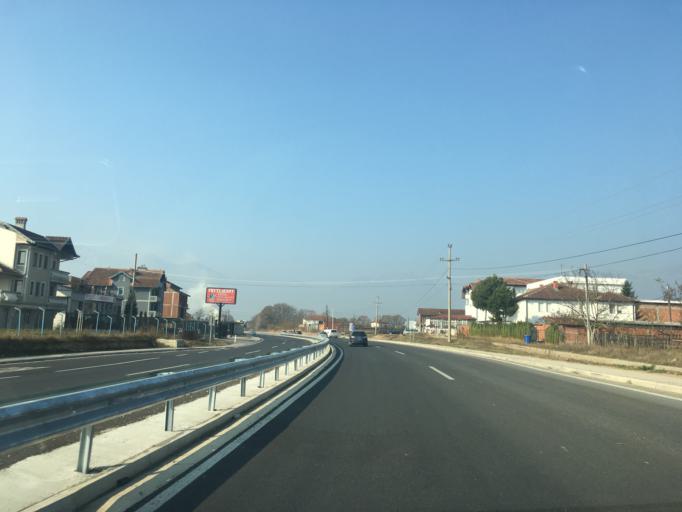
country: XK
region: Pec
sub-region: Komuna e Pejes
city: Dubova (Driloni)
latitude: 42.6546
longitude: 20.3983
